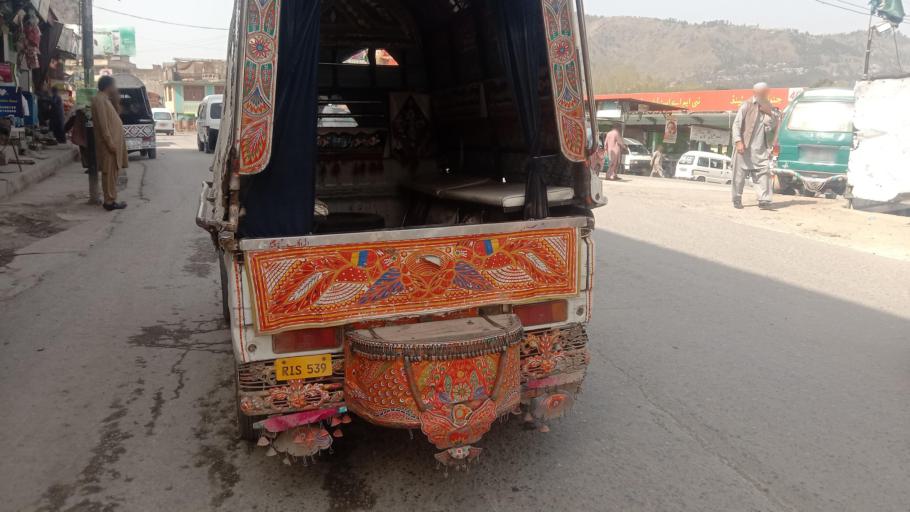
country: PK
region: Khyber Pakhtunkhwa
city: Abbottabad
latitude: 34.1405
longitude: 73.2130
